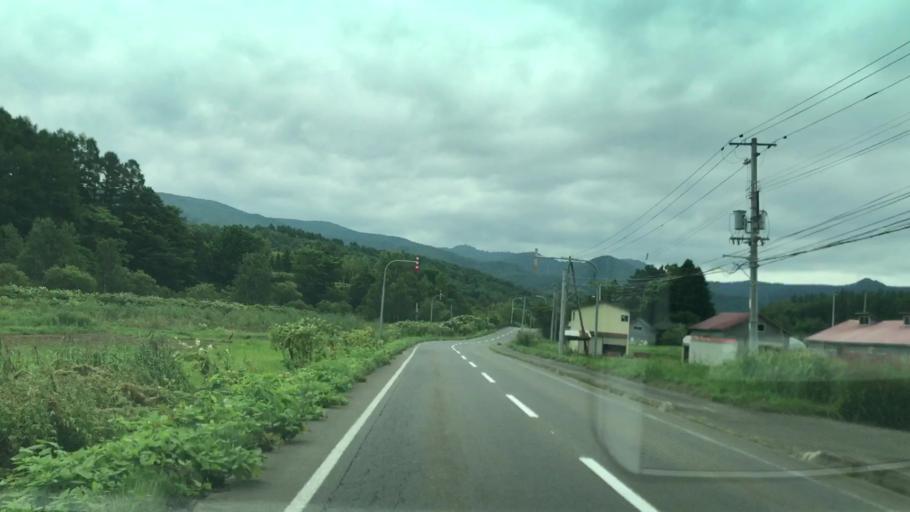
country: JP
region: Hokkaido
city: Yoichi
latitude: 43.0616
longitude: 140.8213
